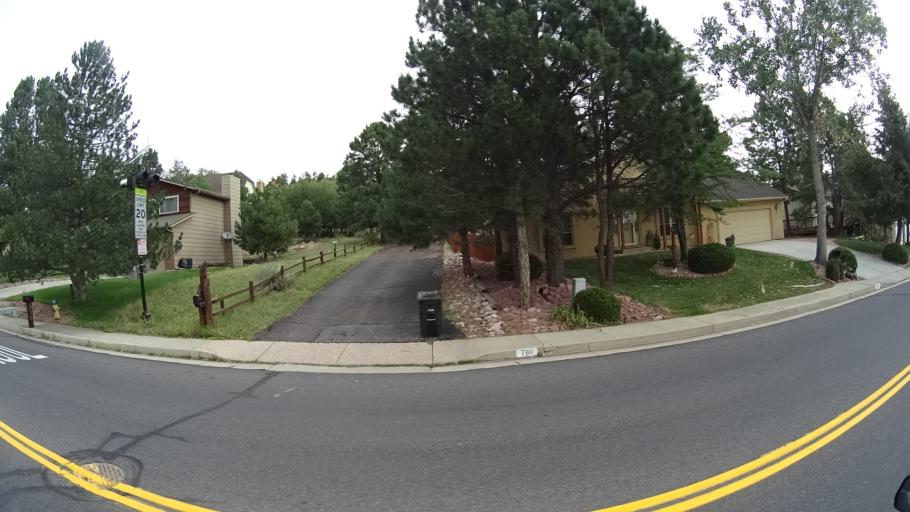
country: US
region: Colorado
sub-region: El Paso County
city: Air Force Academy
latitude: 38.9312
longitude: -104.8424
